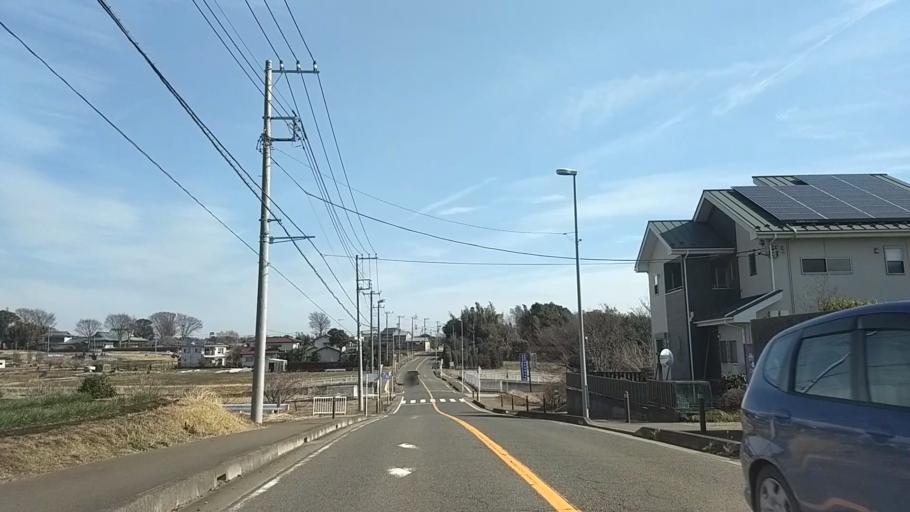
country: JP
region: Kanagawa
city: Chigasaki
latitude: 35.3874
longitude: 139.4083
